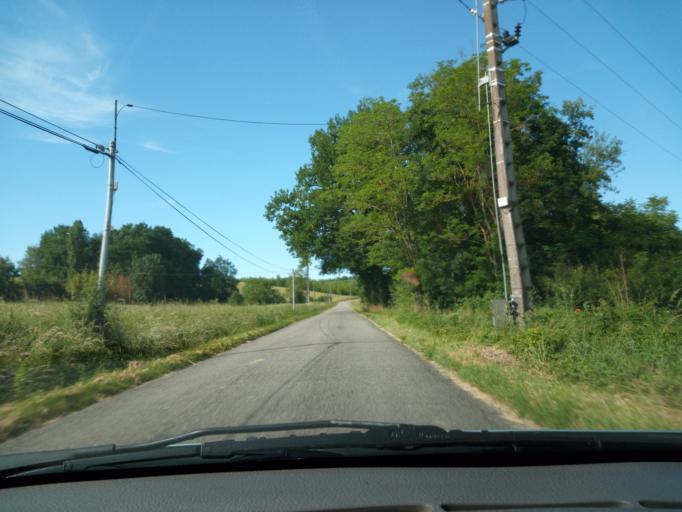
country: FR
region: Midi-Pyrenees
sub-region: Departement du Tarn-et-Garonne
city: Molieres
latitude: 44.2305
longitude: 1.3293
